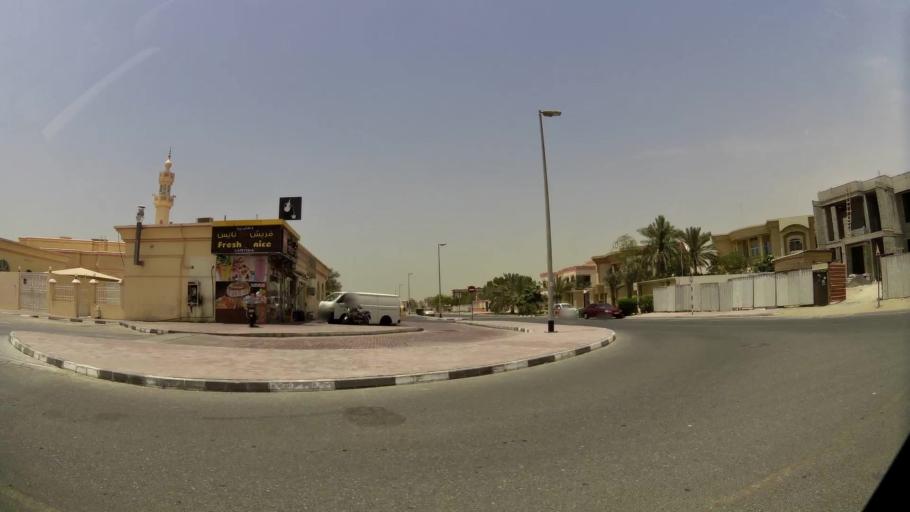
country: AE
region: Ash Shariqah
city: Sharjah
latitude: 25.1913
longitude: 55.3843
